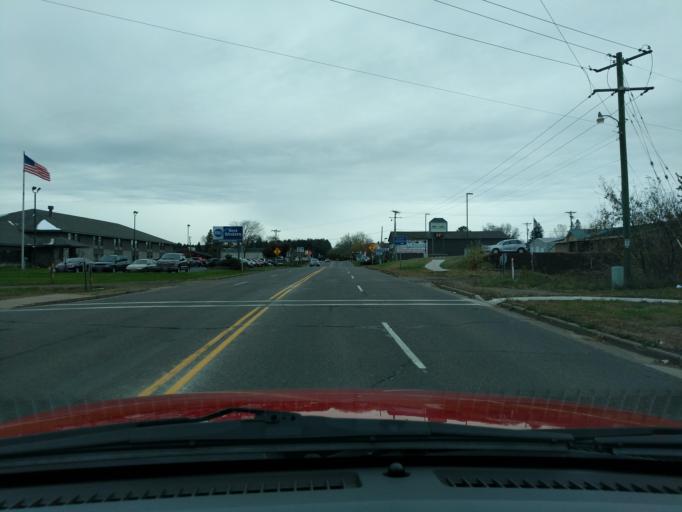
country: US
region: Wisconsin
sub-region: Washburn County
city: Spooner
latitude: 45.8221
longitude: -91.8884
